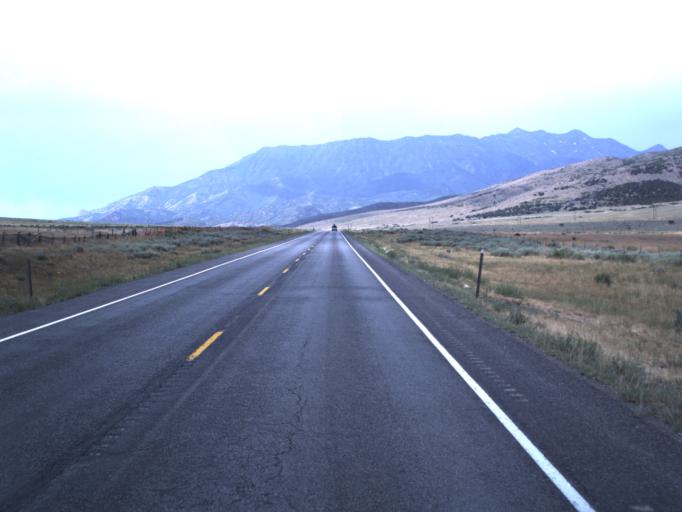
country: US
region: Utah
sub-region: Sanpete County
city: Fountain Green
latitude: 39.6798
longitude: -111.6715
